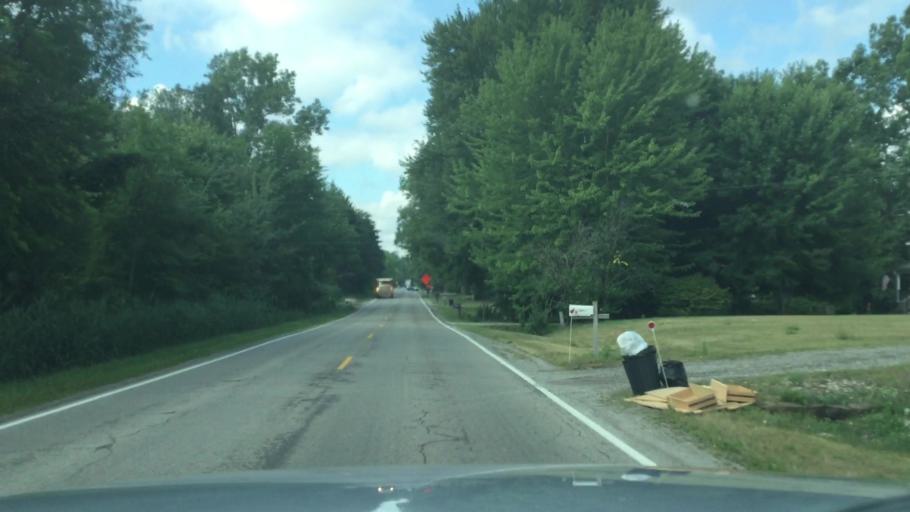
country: US
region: Michigan
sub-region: Genesee County
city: Clio
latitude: 43.2061
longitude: -83.7126
